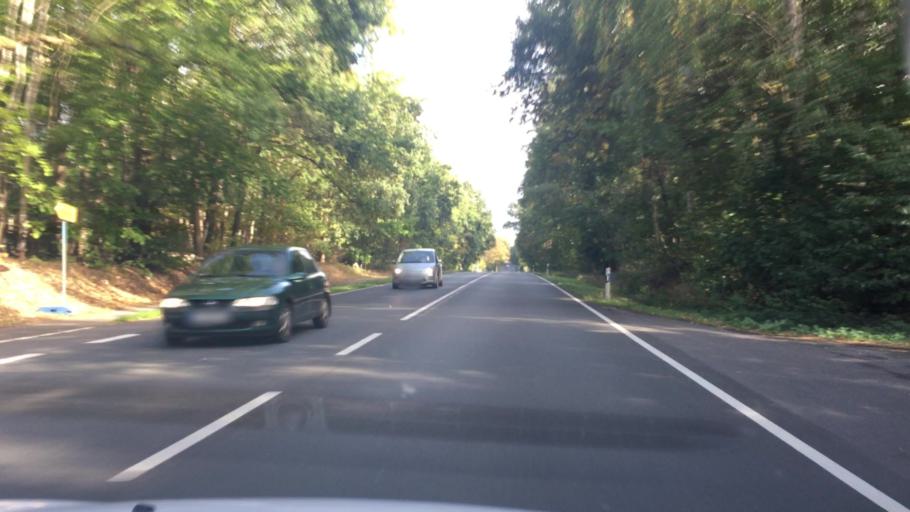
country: DE
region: Lower Saxony
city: Hemsloh
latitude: 52.6118
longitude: 8.5160
